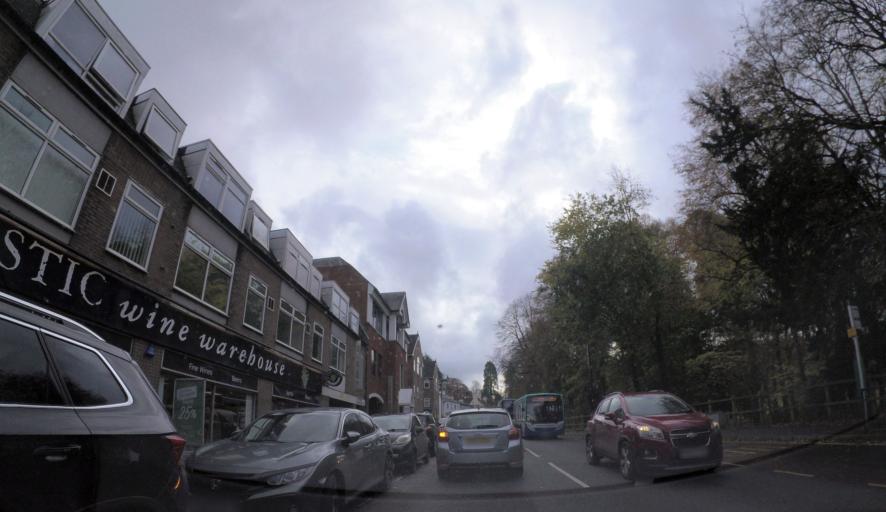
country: GB
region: England
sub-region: Surrey
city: Reigate
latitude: 51.2349
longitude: -0.2041
